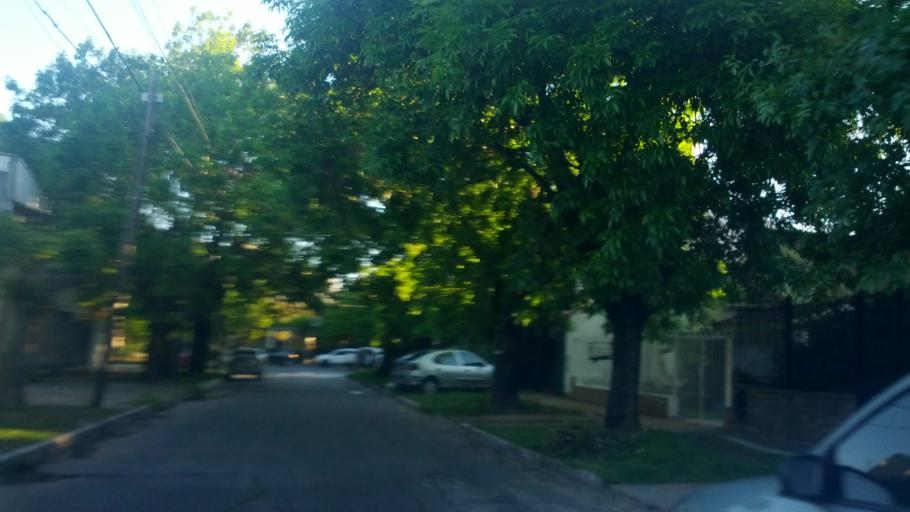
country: AR
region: Buenos Aires
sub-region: Partido de Lomas de Zamora
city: Lomas de Zamora
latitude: -34.7703
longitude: -58.4151
